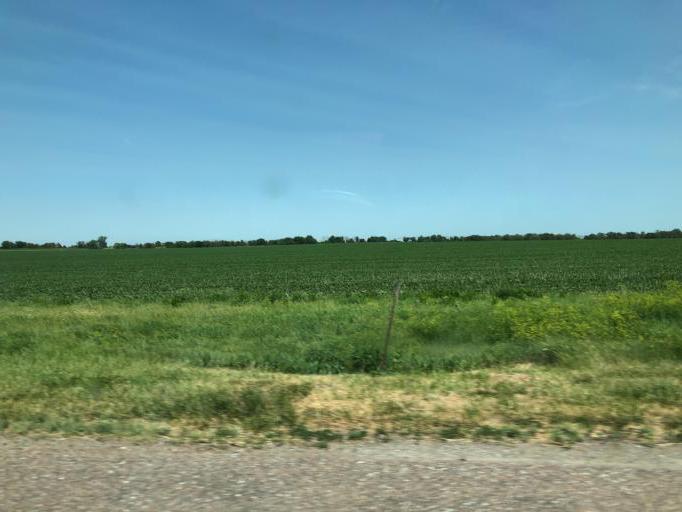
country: US
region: Nebraska
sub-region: Thayer County
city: Hebron
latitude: 40.2885
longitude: -97.5765
